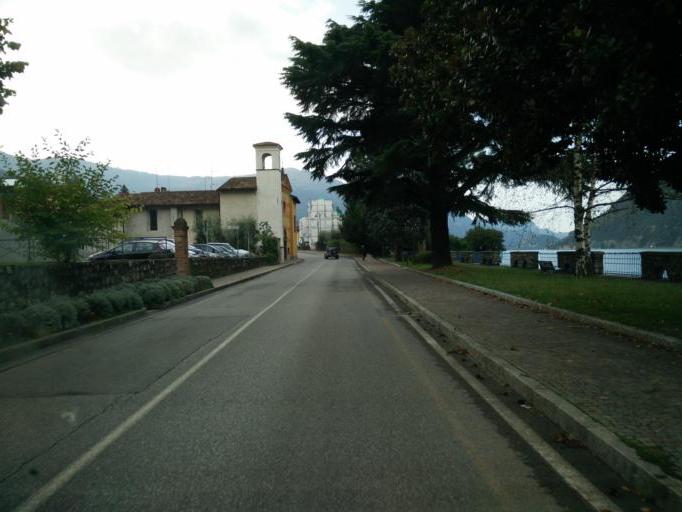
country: IT
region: Lombardy
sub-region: Provincia di Brescia
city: Sale Marasino
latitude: 45.7127
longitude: 10.1099
